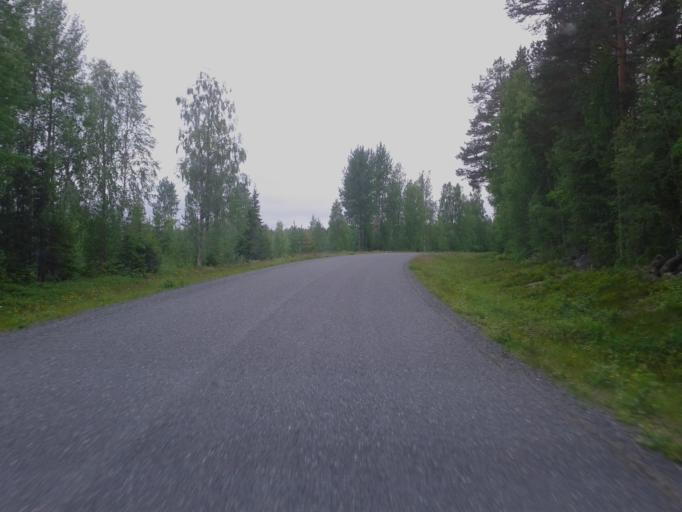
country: SE
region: Vaesterbotten
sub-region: Skelleftea Kommun
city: Storvik
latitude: 65.0047
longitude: 20.7495
